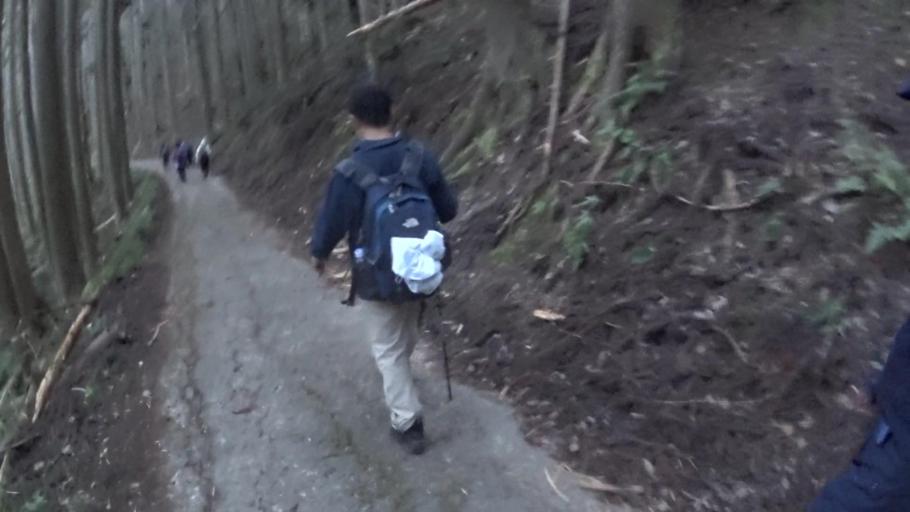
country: JP
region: Kyoto
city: Kameoka
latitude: 35.0448
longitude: 135.6555
